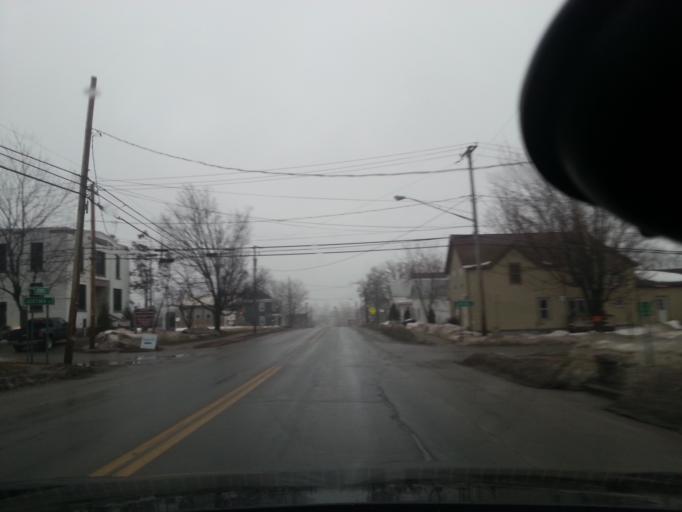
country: US
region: New York
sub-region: St. Lawrence County
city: Ogdensburg
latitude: 44.6193
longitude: -75.4093
